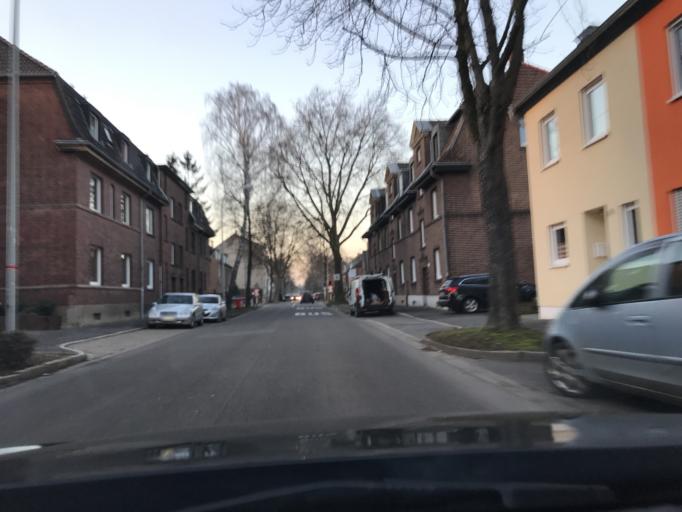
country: DE
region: North Rhine-Westphalia
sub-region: Regierungsbezirk Dusseldorf
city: Krefeld
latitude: 51.3332
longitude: 6.6114
